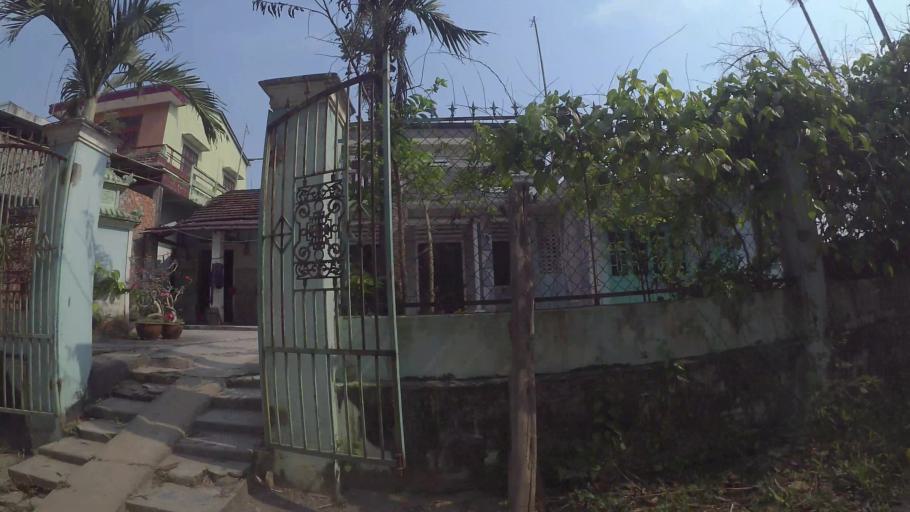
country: VN
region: Da Nang
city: Cam Le
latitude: 15.9967
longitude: 108.2194
